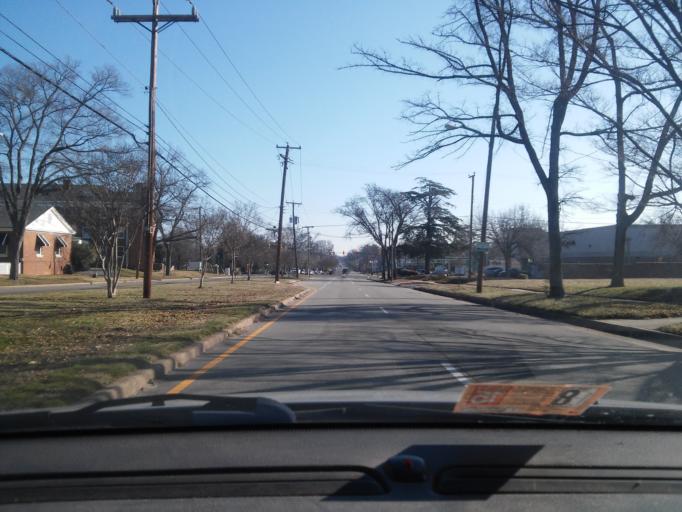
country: US
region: Virginia
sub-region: City of Richmond
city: Richmond
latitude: 37.5722
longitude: -77.4469
